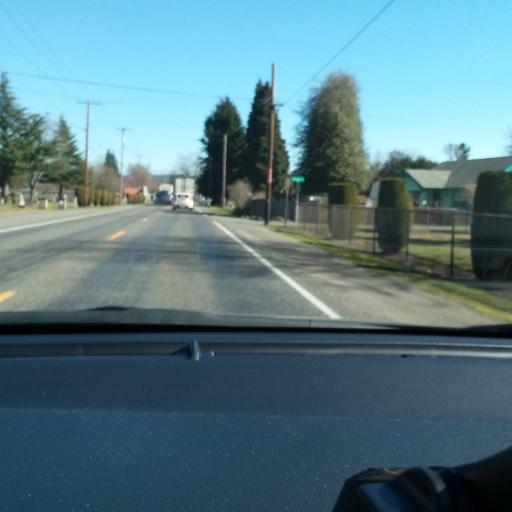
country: US
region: Washington
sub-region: Pierce County
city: North Puyallup
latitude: 47.2047
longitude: -122.2640
